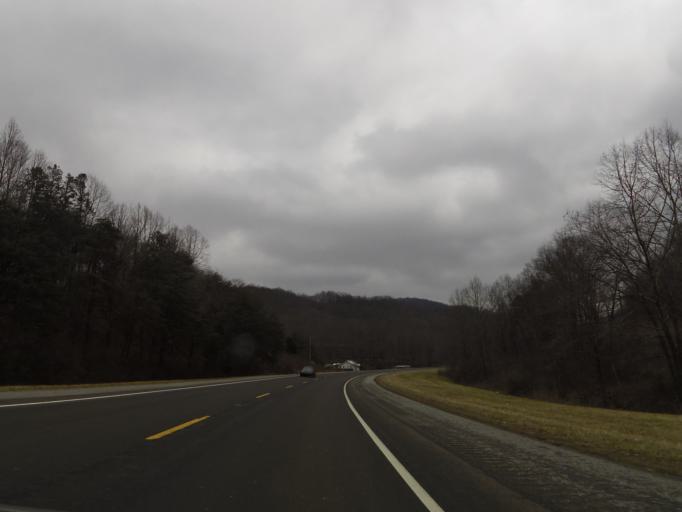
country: US
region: Tennessee
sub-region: Campbell County
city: Caryville
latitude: 36.3926
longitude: -84.3399
